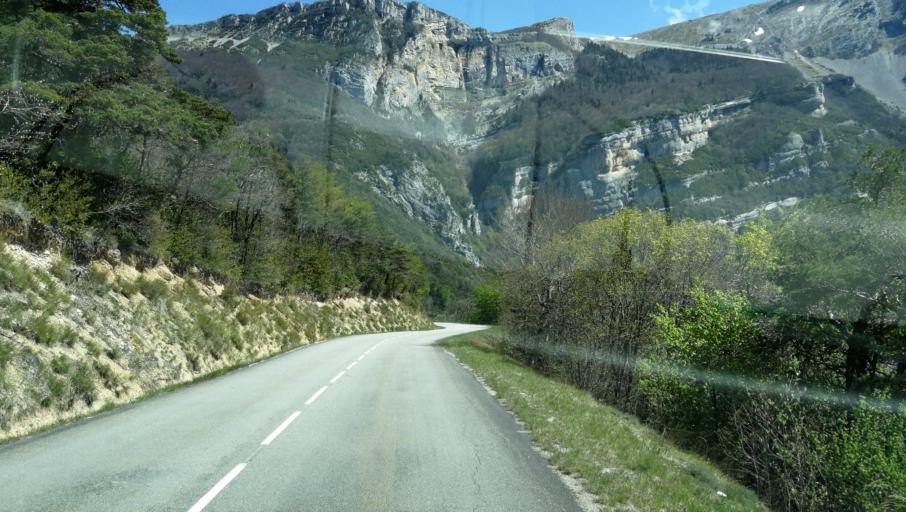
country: FR
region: Rhone-Alpes
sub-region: Departement de la Drome
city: Die
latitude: 44.8233
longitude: 5.3911
